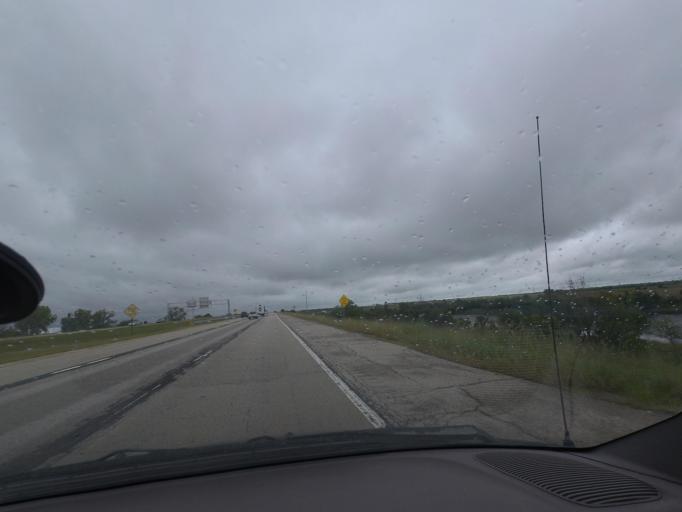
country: US
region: Illinois
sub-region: Macon County
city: Harristown
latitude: 39.8496
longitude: -89.0453
